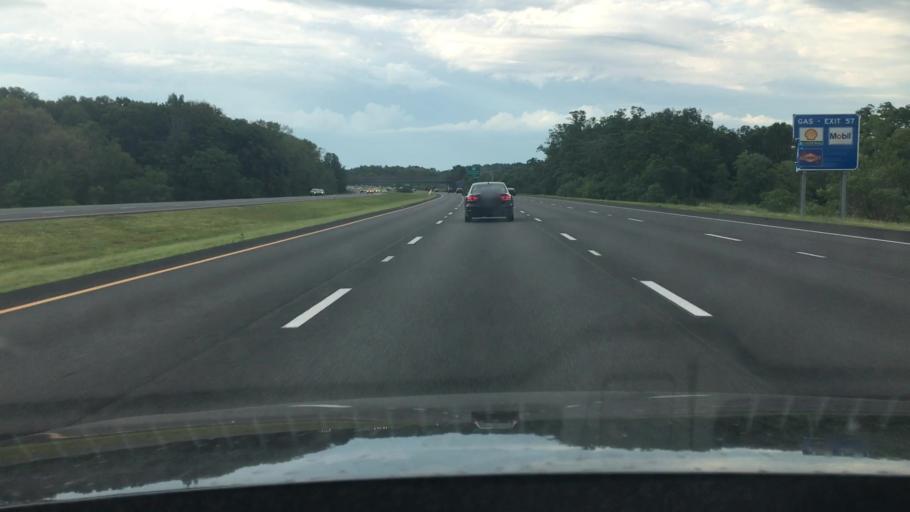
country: US
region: Massachusetts
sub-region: Essex County
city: Newburyport
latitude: 42.7977
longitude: -70.9165
